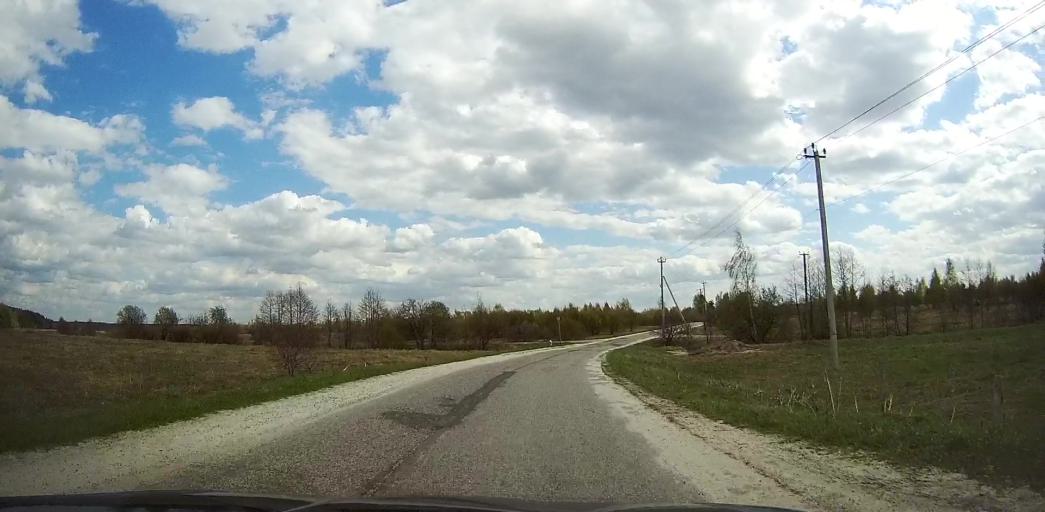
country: RU
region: Moskovskaya
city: Davydovo
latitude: 55.6356
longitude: 38.7822
